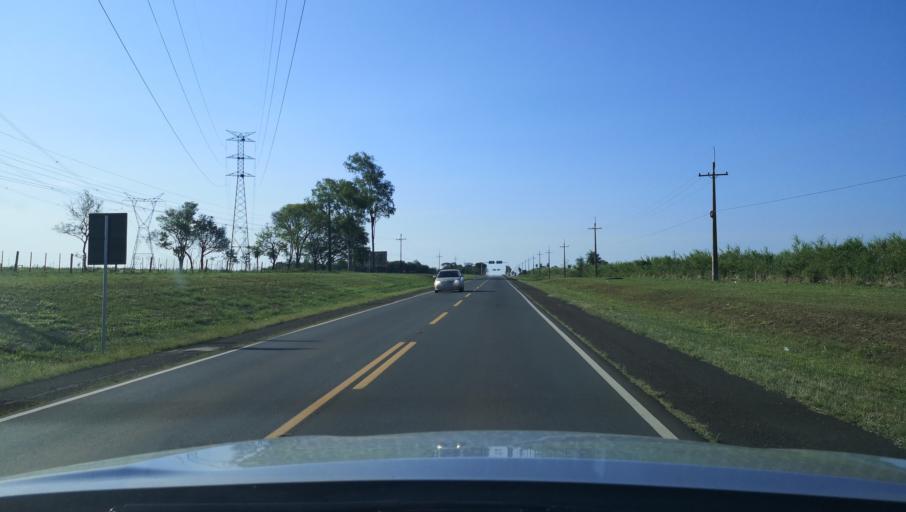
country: PY
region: Misiones
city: Santa Maria
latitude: -26.7882
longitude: -57.0254
